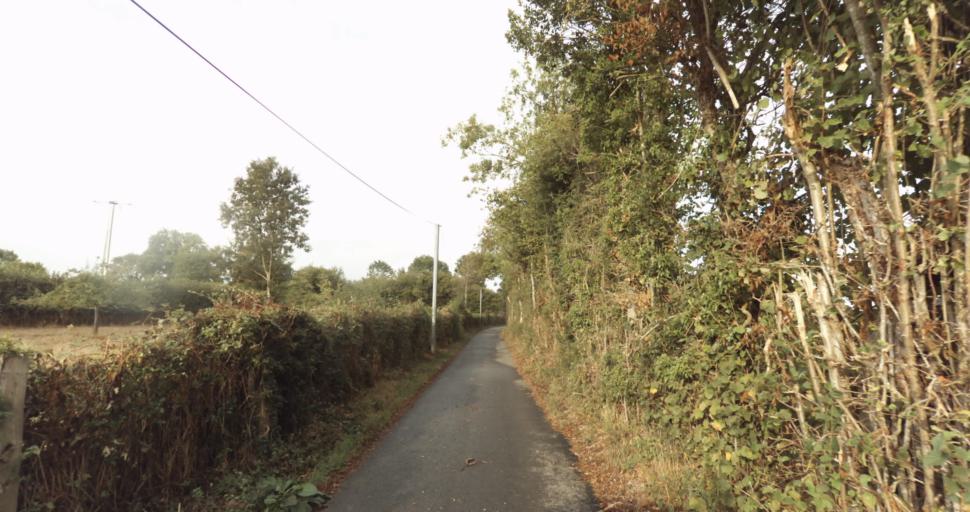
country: FR
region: Lower Normandy
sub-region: Departement de l'Orne
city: Vimoutiers
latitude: 48.9025
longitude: 0.2553
